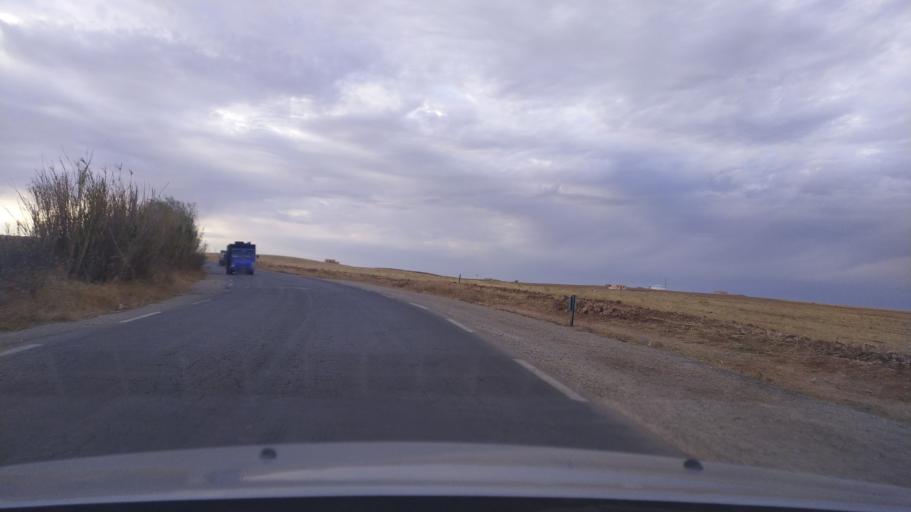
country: DZ
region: Tiaret
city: Frenda
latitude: 34.9852
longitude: 1.1407
